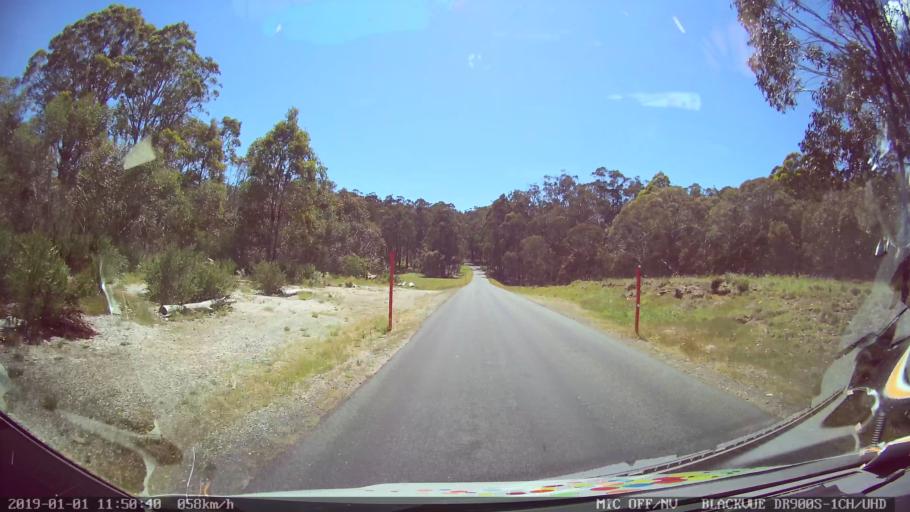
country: AU
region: New South Wales
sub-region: Snowy River
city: Jindabyne
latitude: -35.8899
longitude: 148.4230
